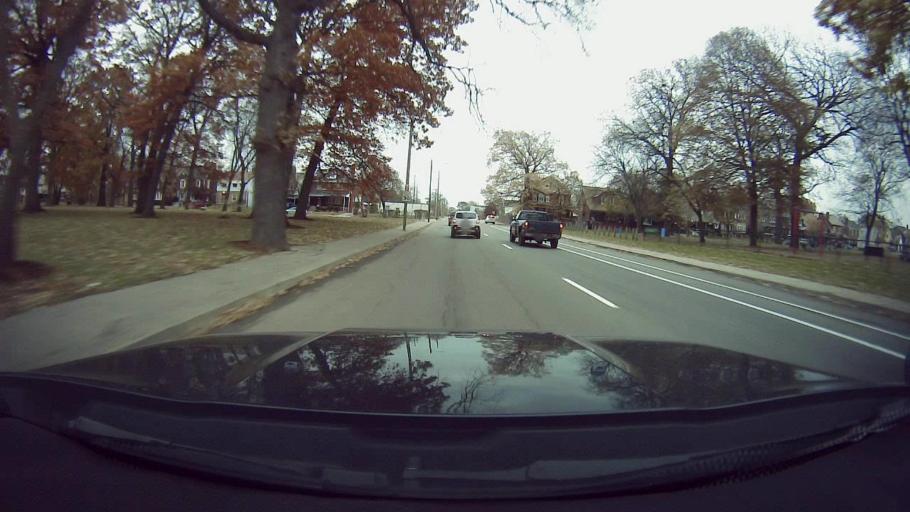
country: US
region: Michigan
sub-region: Wayne County
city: Hamtramck
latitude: 42.3759
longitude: -83.0060
